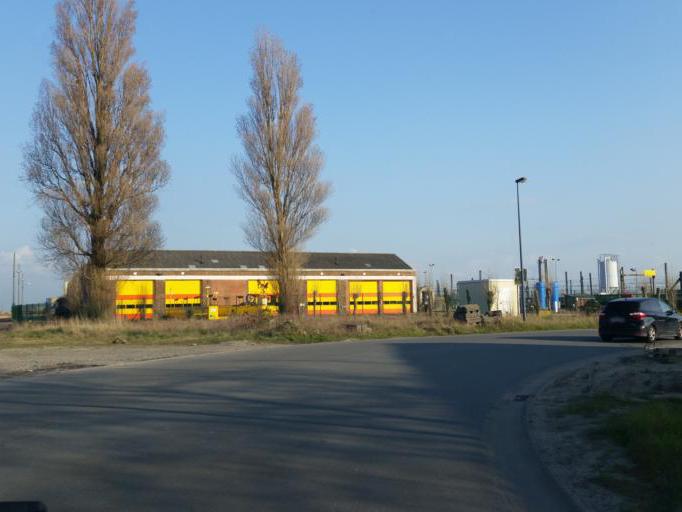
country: BE
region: Flanders
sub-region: Provincie West-Vlaanderen
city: Ostend
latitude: 51.2181
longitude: 2.9487
